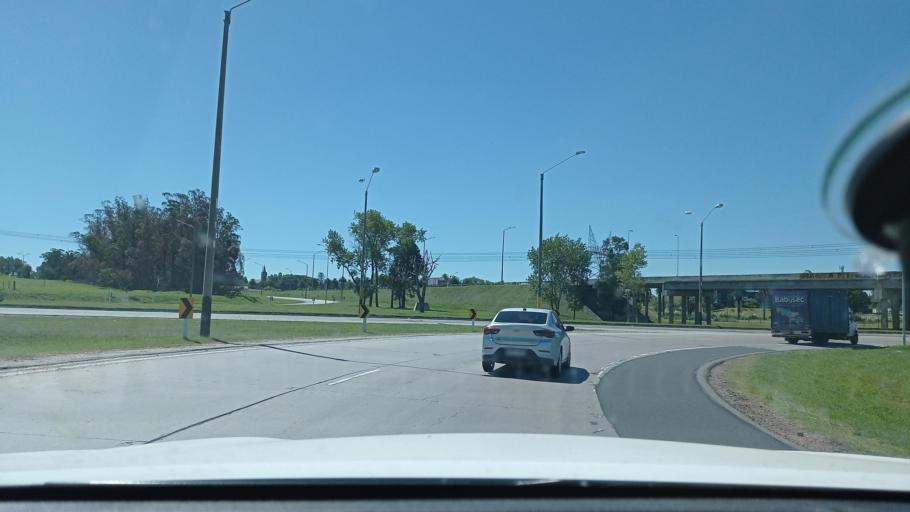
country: UY
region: Canelones
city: Colonia Nicolich
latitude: -34.7952
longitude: -56.0741
